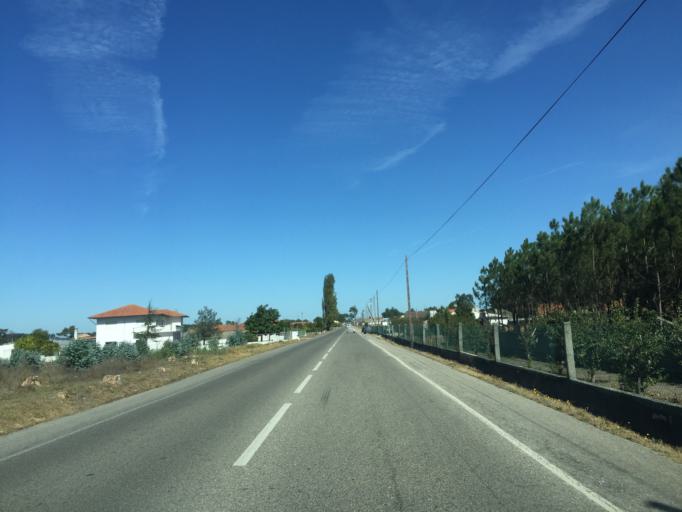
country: PT
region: Coimbra
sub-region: Figueira da Foz
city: Alhadas
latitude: 40.2484
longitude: -8.7864
